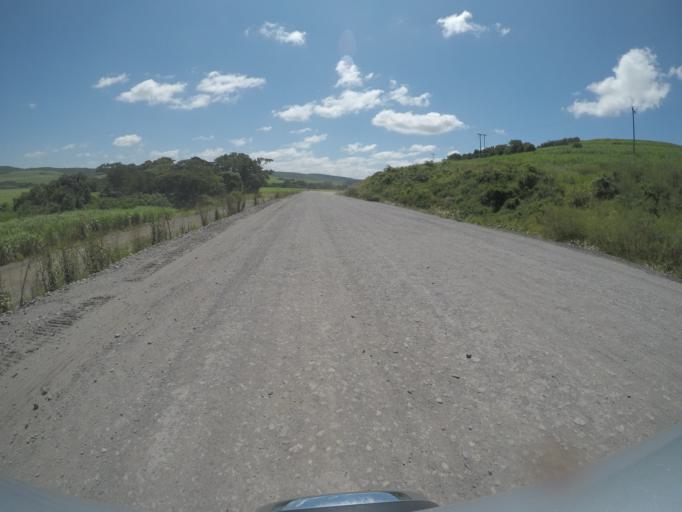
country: ZA
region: KwaZulu-Natal
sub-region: uThungulu District Municipality
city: Empangeni
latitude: -28.6563
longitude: 31.7704
